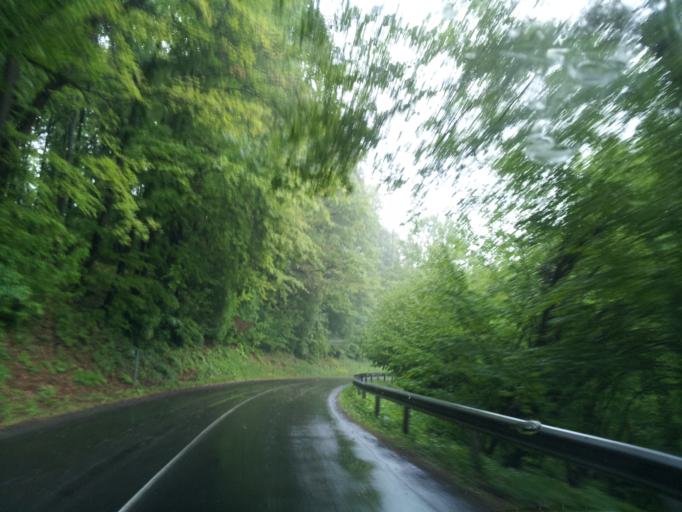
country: HU
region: Baranya
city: Komlo
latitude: 46.2169
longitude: 18.3012
